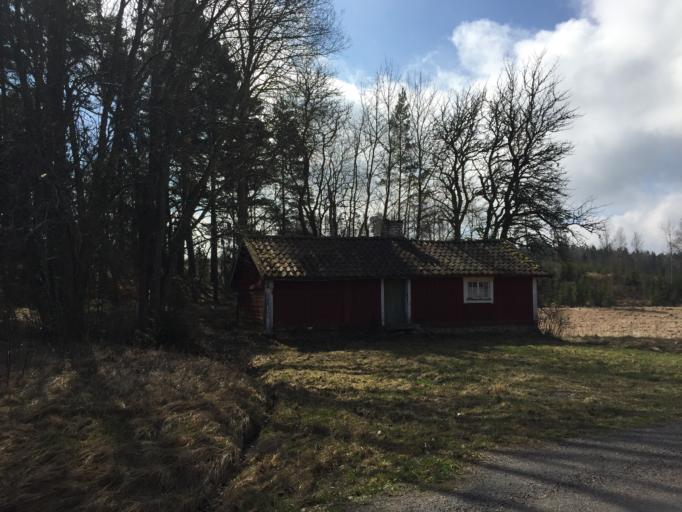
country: SE
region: Soedermanland
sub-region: Gnesta Kommun
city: Gnesta
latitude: 59.0335
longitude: 17.2181
